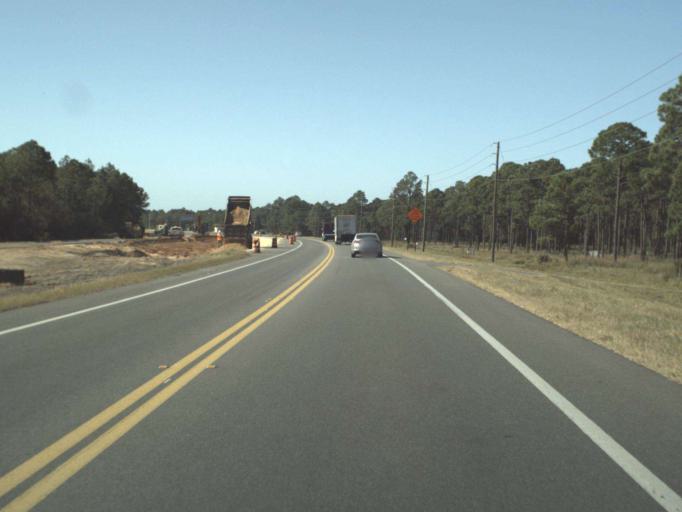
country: US
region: Florida
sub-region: Walton County
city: Freeport
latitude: 30.4411
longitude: -86.1461
